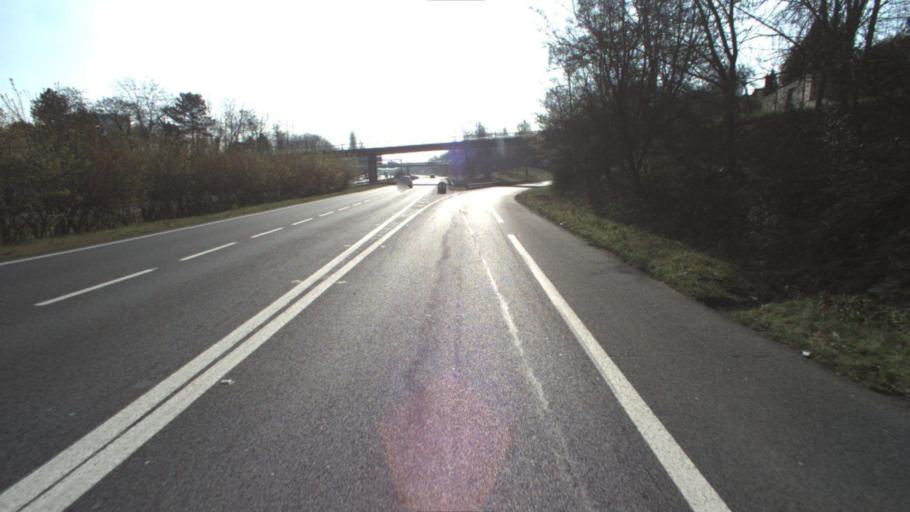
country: FR
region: Ile-de-France
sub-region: Departement de l'Essonne
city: Linas
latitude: 48.6271
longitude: 2.2589
